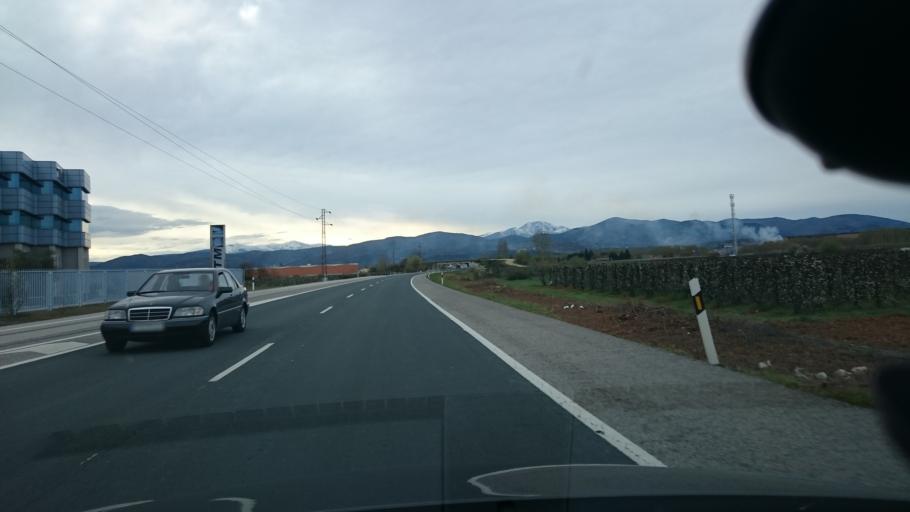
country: ES
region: Castille and Leon
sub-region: Provincia de Leon
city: Carracedelo
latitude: 42.5635
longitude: -6.7168
